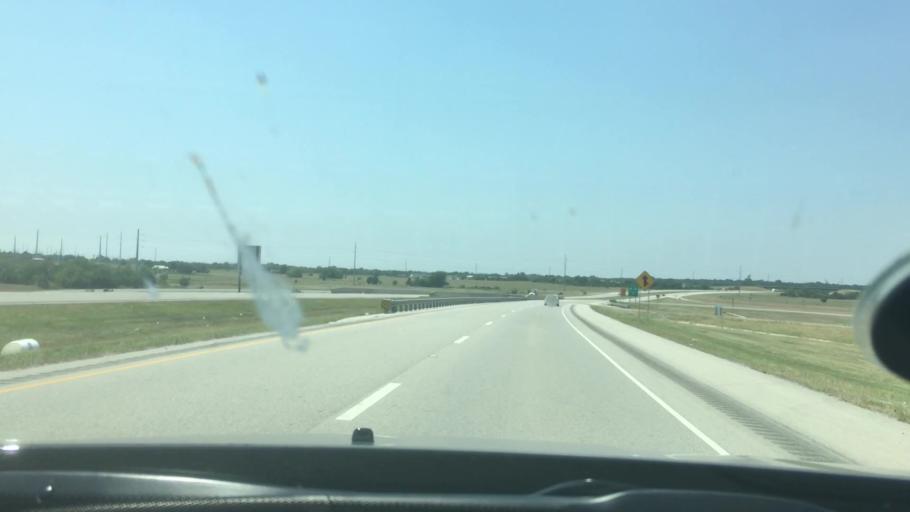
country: US
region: Oklahoma
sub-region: Bryan County
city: Calera
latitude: 33.9682
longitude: -96.4143
